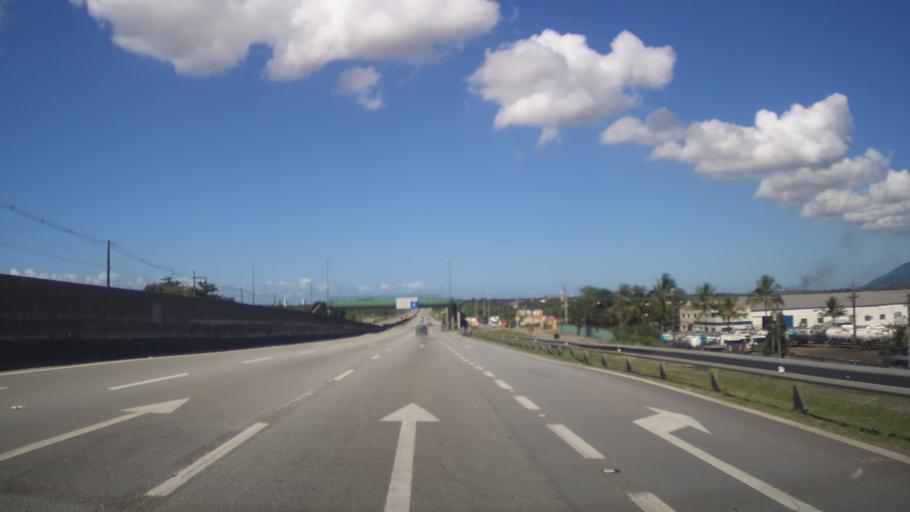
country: BR
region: Sao Paulo
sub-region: Praia Grande
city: Praia Grande
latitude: -23.9895
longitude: -46.4945
